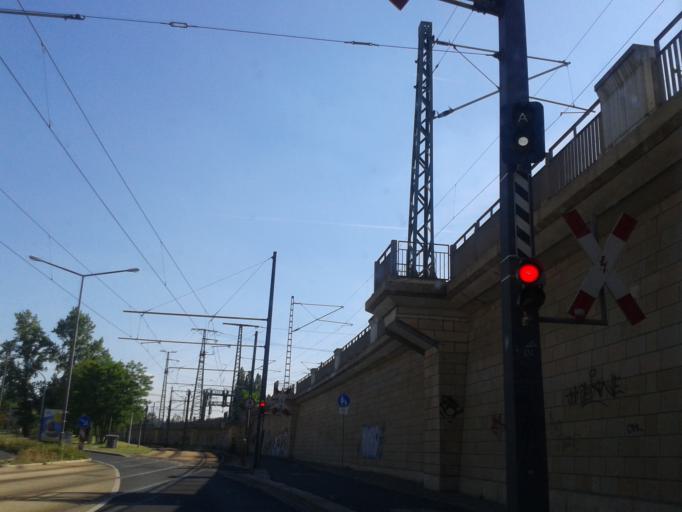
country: DE
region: Saxony
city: Dresden
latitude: 51.0520
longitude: 13.7204
